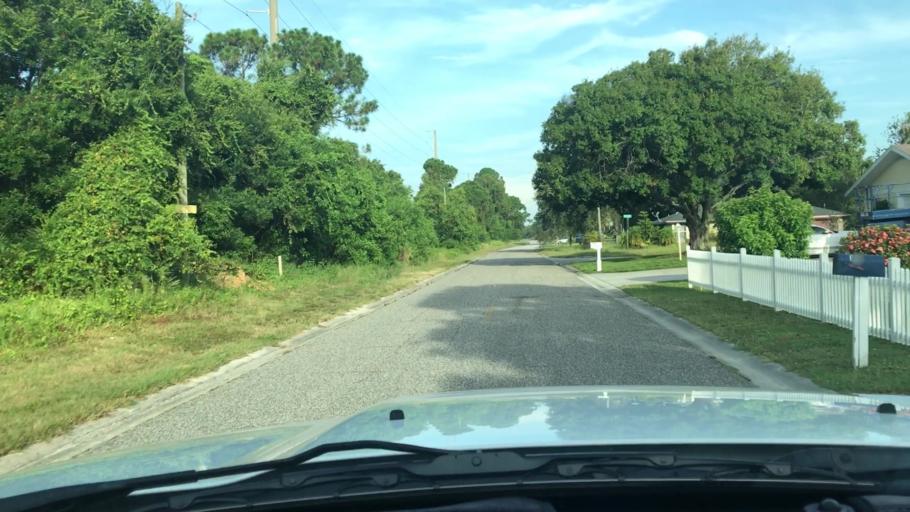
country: US
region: Florida
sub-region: Saint Lucie County
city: Lakewood Park
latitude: 27.5580
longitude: -80.3965
